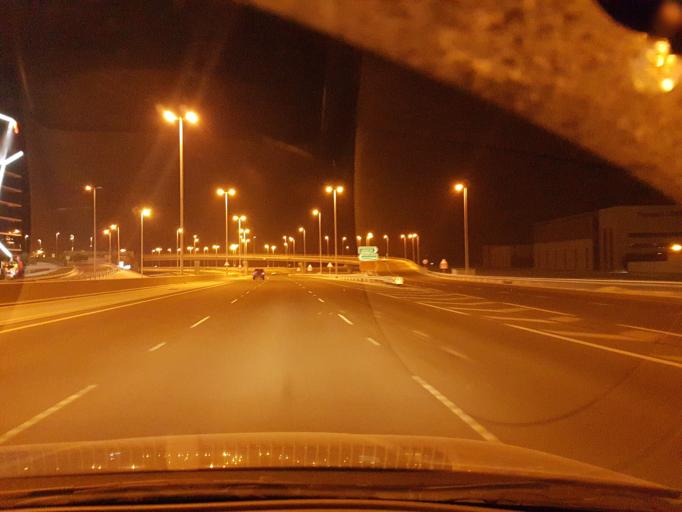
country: BH
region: Muharraq
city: Al Muharraq
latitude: 26.2512
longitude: 50.5844
